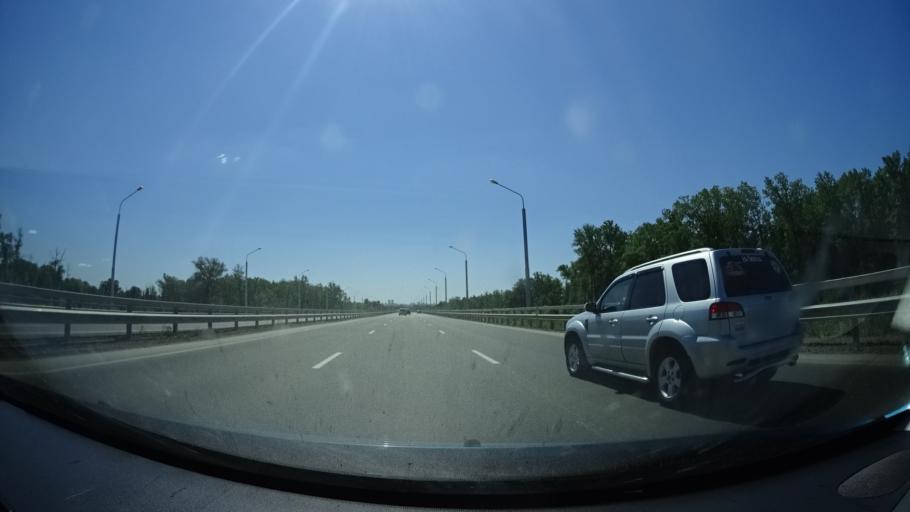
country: RU
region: Bashkortostan
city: Mikhaylovka
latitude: 54.7924
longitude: 55.9047
